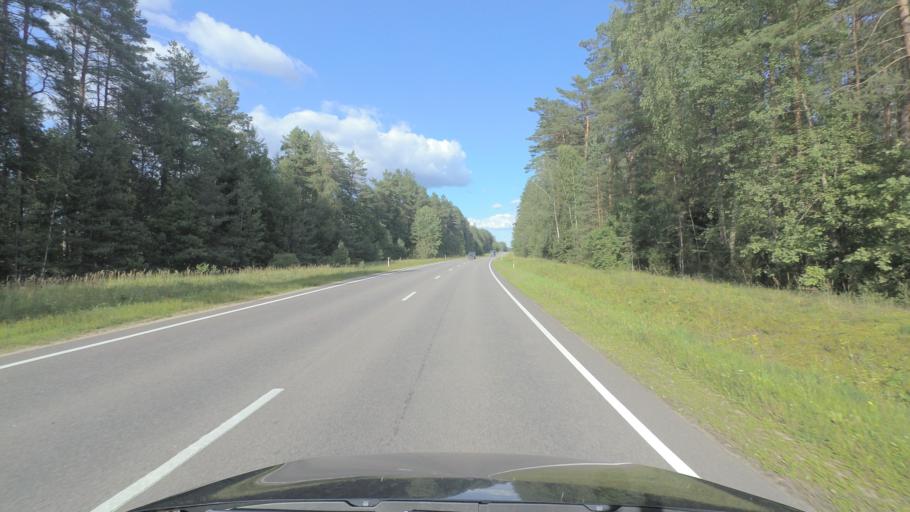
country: LT
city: Pabrade
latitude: 54.9537
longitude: 25.6726
